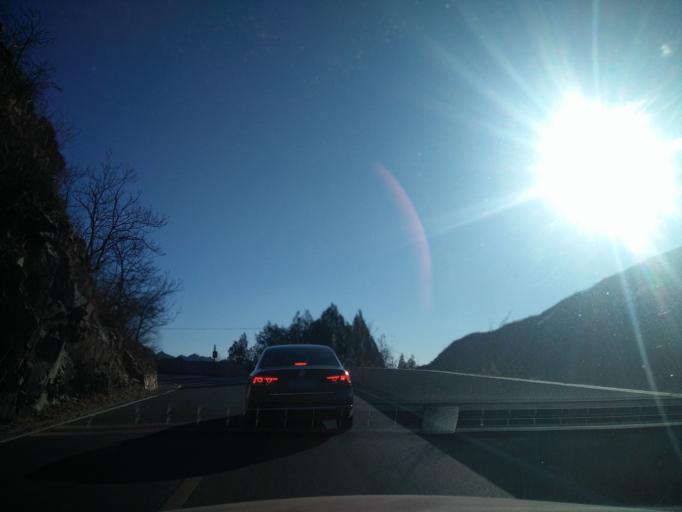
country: CN
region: Beijing
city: Wangping
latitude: 40.0070
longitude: 115.9696
